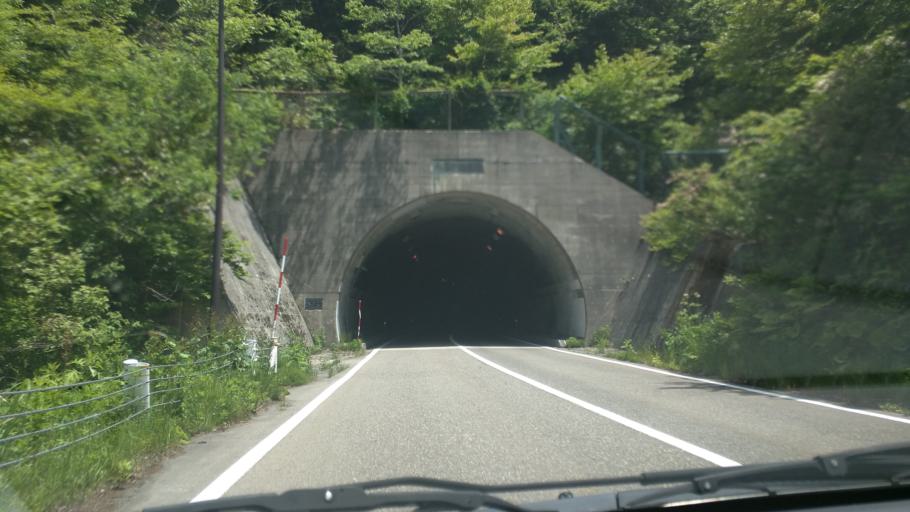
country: JP
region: Fukushima
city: Kitakata
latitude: 37.3591
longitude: 139.8715
